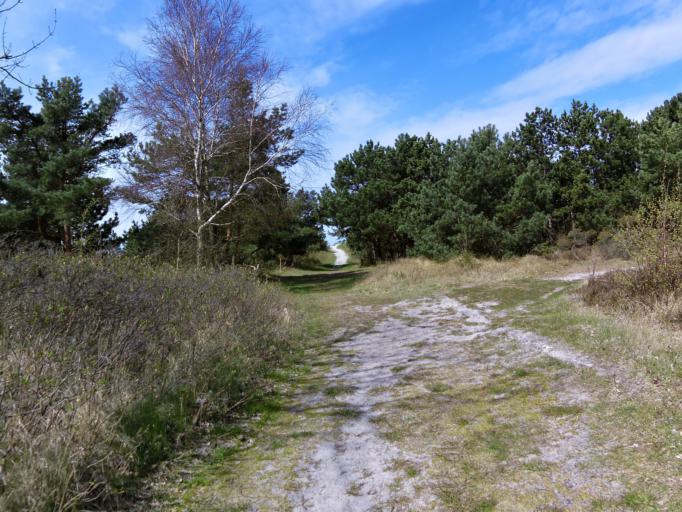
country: DE
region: Mecklenburg-Vorpommern
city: Hiddensee
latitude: 54.5461
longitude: 13.0948
